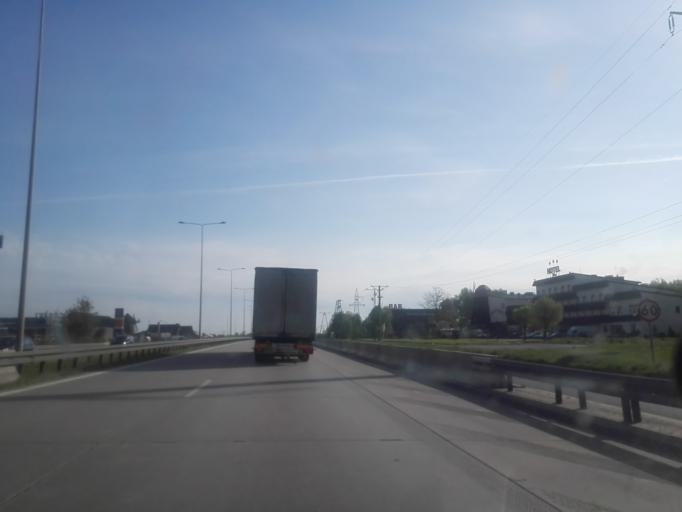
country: PL
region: Lodz Voivodeship
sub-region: Powiat piotrkowski
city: Wolborz
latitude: 51.4585
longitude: 19.7784
